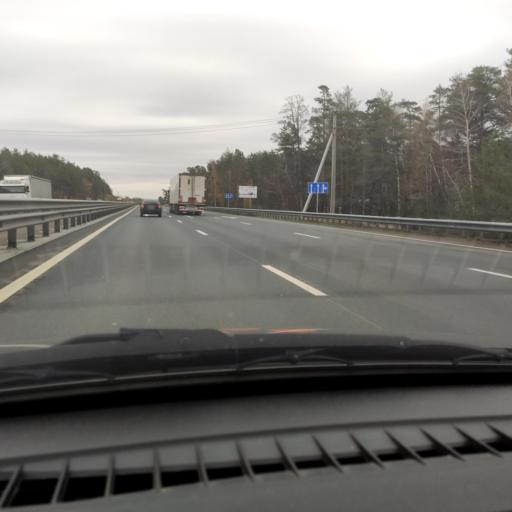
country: RU
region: Samara
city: Zhigulevsk
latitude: 53.5053
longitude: 49.5530
